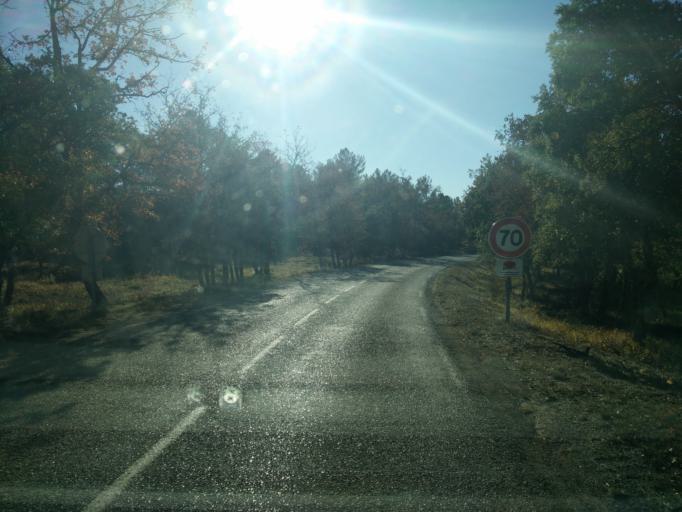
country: FR
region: Provence-Alpes-Cote d'Azur
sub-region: Departement du Var
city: Aups
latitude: 43.6043
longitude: 6.2196
